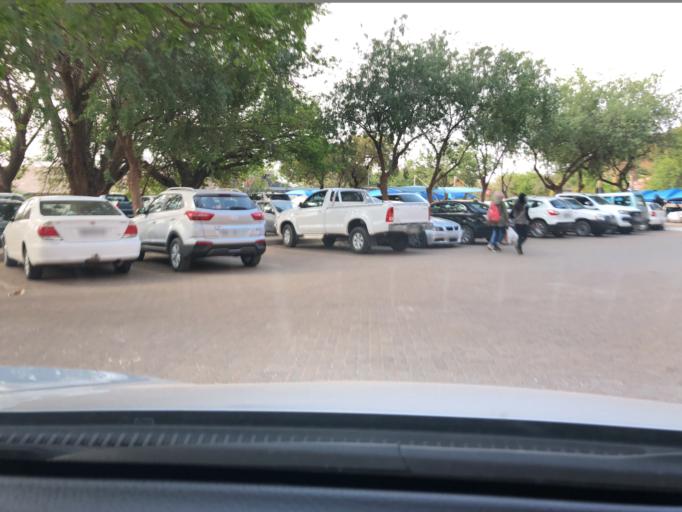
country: ZA
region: Limpopo
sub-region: Capricorn District Municipality
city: Mankoeng
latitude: -23.8879
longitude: 29.7377
